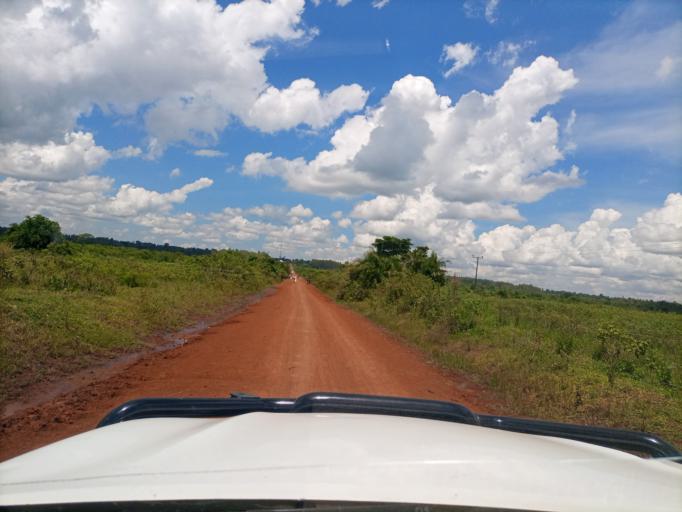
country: UG
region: Eastern Region
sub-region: Busia District
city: Busia
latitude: 0.6256
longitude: 33.9897
